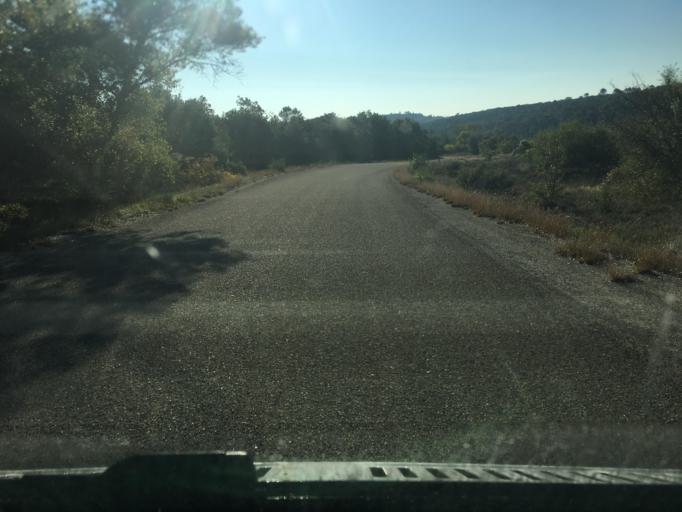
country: FR
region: Languedoc-Roussillon
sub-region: Departement du Gard
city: Goudargues
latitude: 44.1671
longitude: 4.3503
